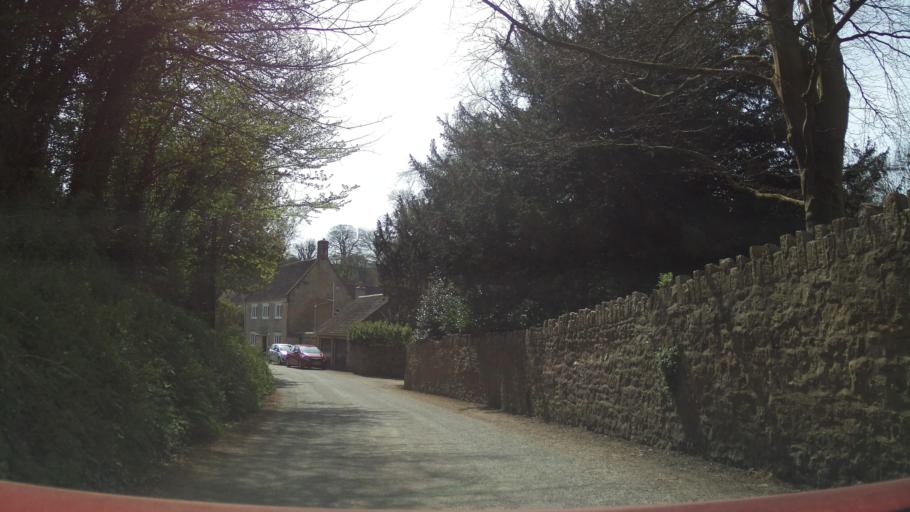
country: GB
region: England
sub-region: Dorset
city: Sherborne
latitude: 50.9861
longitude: -2.5391
